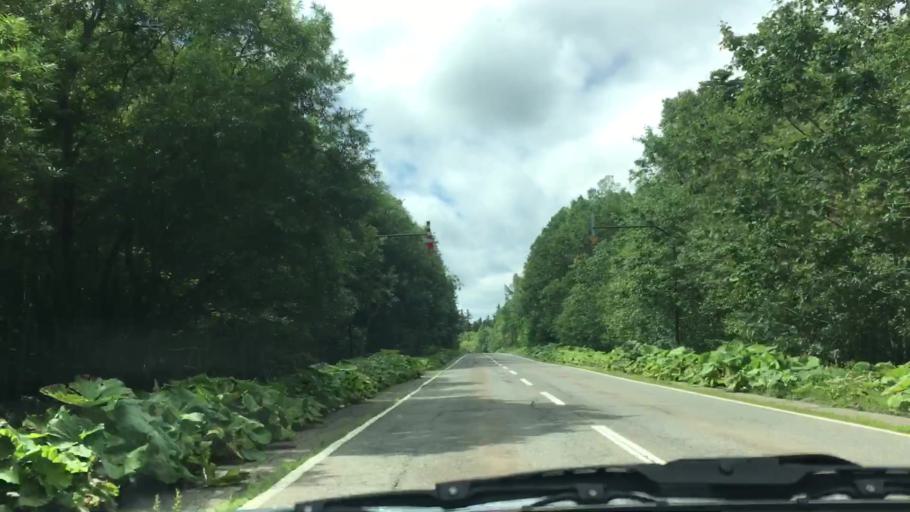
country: JP
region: Hokkaido
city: Kitami
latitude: 43.4289
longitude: 143.9900
